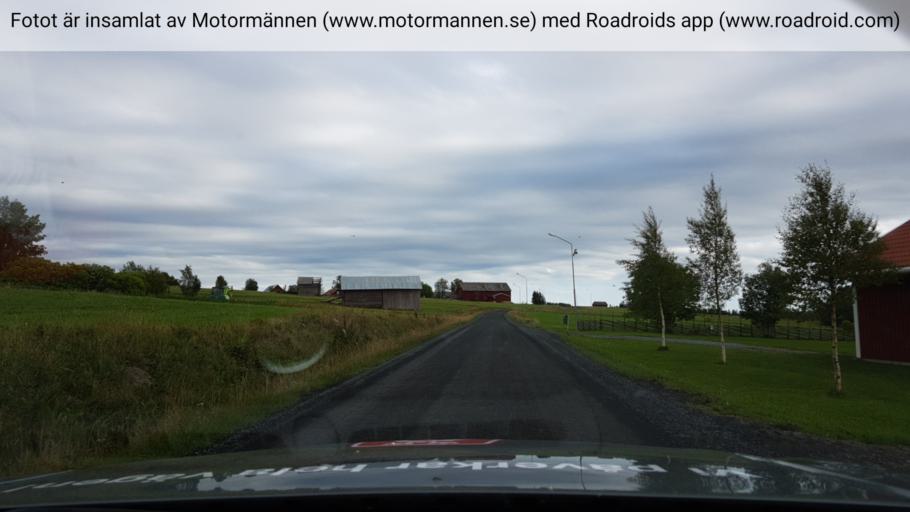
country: SE
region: Jaemtland
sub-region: Krokoms Kommun
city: Valla
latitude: 63.3543
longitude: 13.9768
